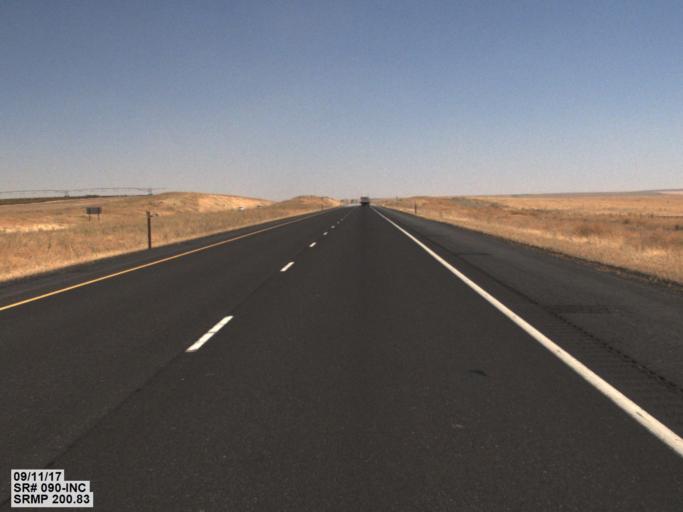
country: US
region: Washington
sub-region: Grant County
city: Warden
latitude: 47.0859
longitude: -118.7921
